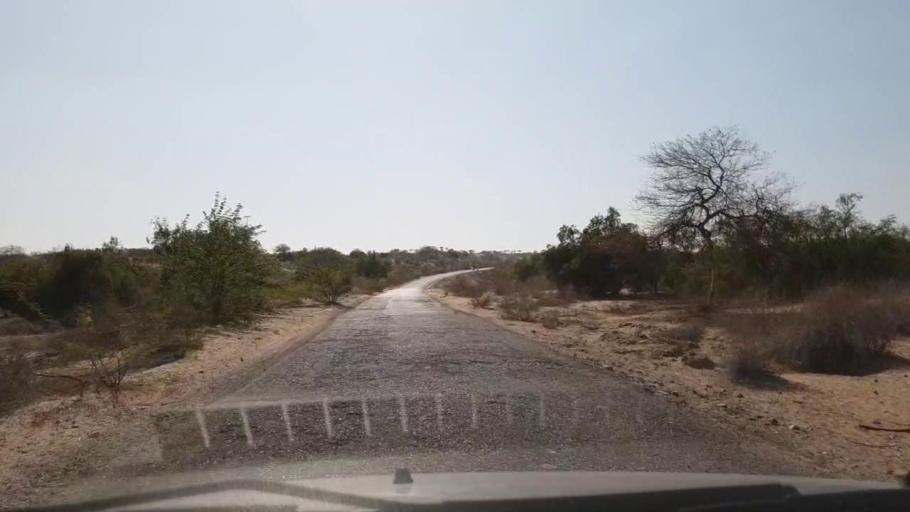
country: PK
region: Sindh
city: Mithi
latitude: 24.6361
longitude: 69.7426
